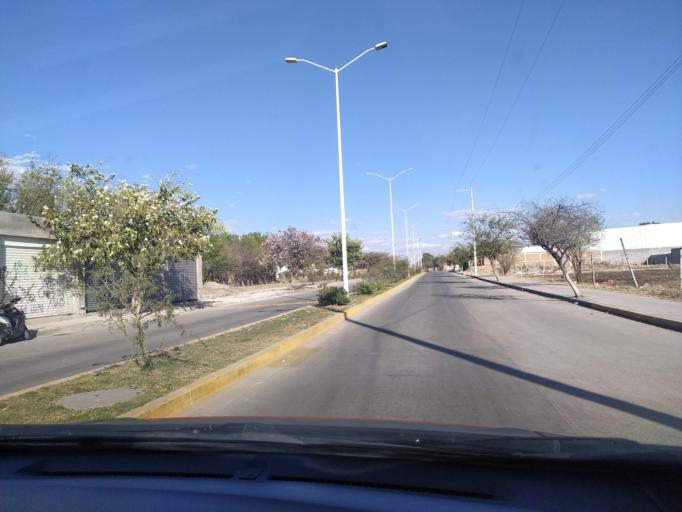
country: LA
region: Oudomxai
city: Muang La
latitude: 21.0174
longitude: 101.8427
